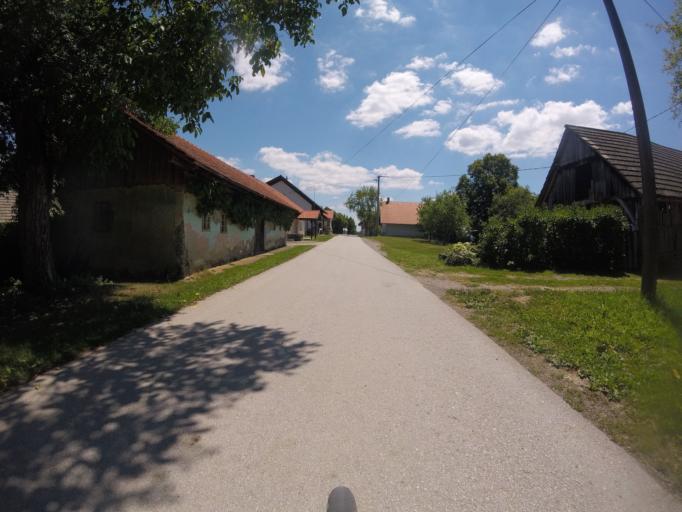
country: SI
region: Metlika
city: Metlika
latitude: 45.6926
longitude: 15.3941
